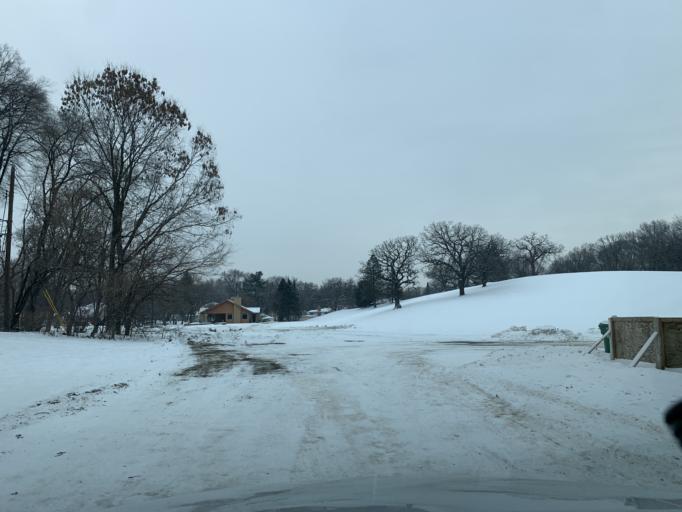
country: US
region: Minnesota
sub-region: Hennepin County
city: Saint Louis Park
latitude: 44.9217
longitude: -93.3438
